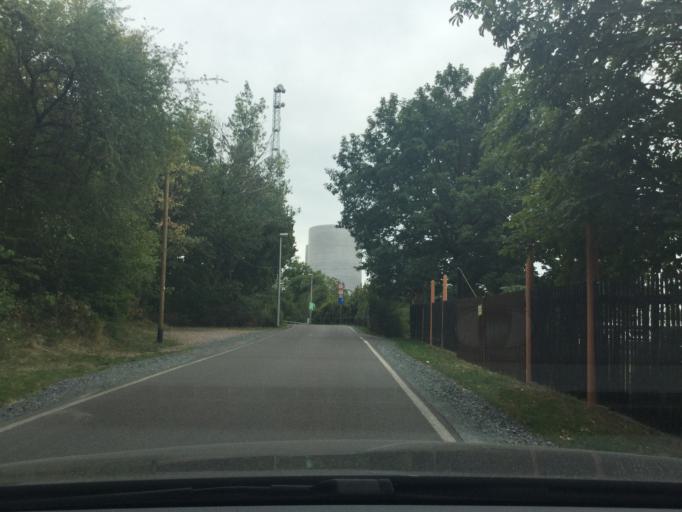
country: DE
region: Saxony
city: Coswig
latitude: 51.0868
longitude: 13.6043
